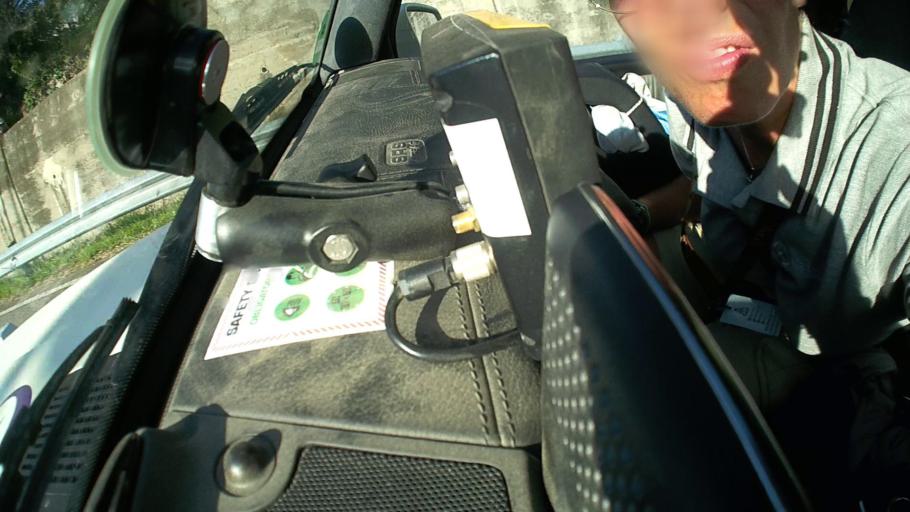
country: AR
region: Cordoba
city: Villa Carlos Paz
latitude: -31.4008
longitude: -64.4653
